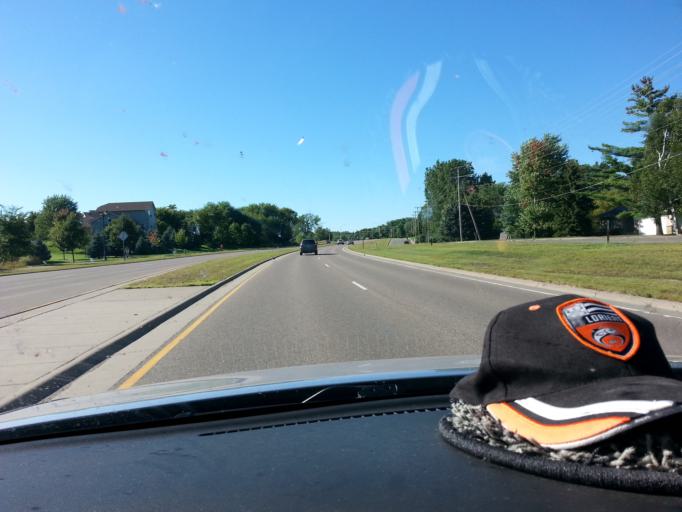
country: US
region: Minnesota
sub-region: Scott County
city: Prior Lake
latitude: 44.7079
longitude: -93.4130
